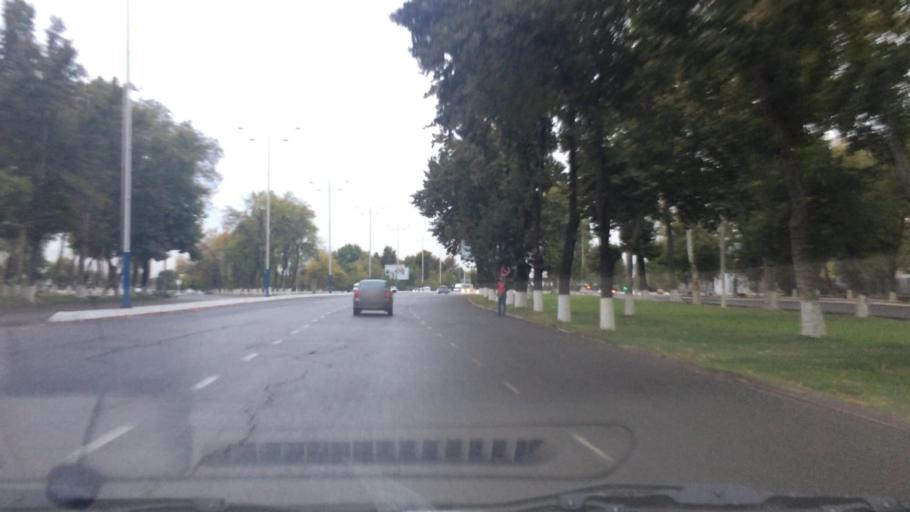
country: UZ
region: Toshkent Shahri
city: Tashkent
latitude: 41.2597
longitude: 69.1961
